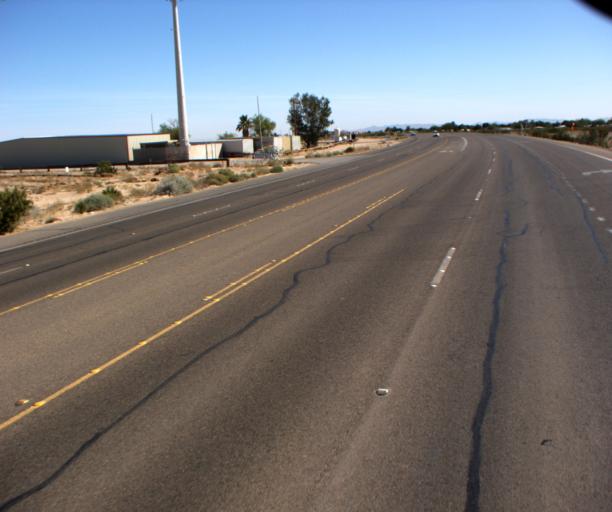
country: US
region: Arizona
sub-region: Yuma County
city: Somerton
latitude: 32.5970
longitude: -114.6688
